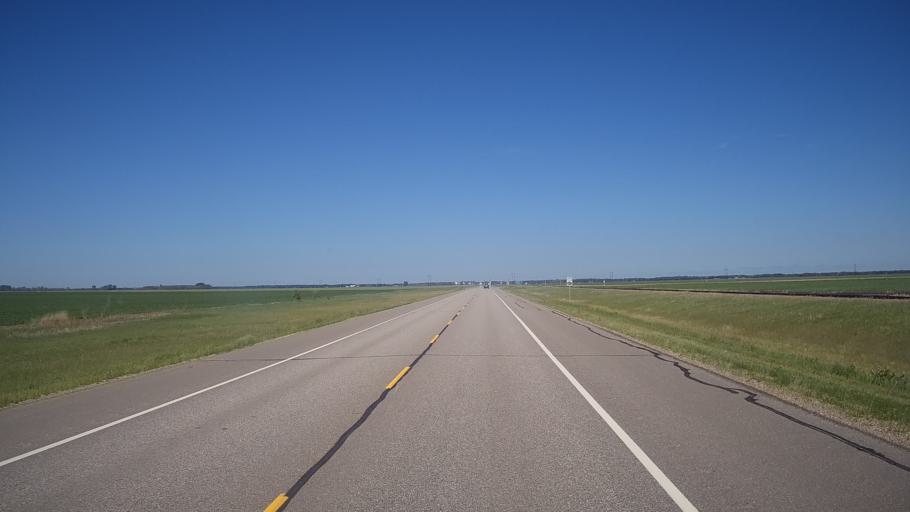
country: CA
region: Manitoba
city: Portage la Prairie
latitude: 50.1043
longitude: -98.5389
